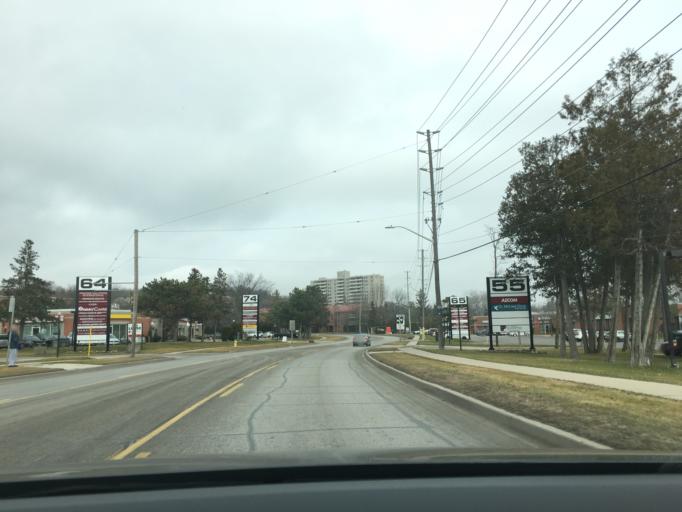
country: CA
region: Ontario
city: Barrie
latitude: 44.3823
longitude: -79.7122
